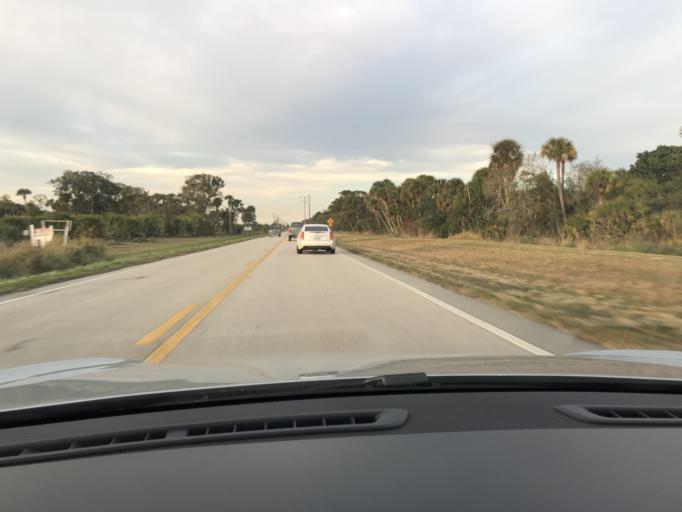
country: US
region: Florida
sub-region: Saint Lucie County
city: Lakewood Park
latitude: 27.5704
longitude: -80.4308
